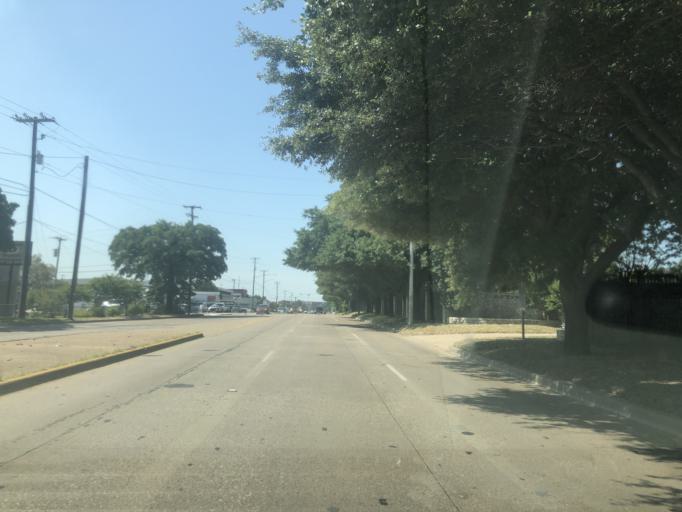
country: US
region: Texas
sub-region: Tarrant County
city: River Oaks
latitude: 32.7629
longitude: -97.3611
